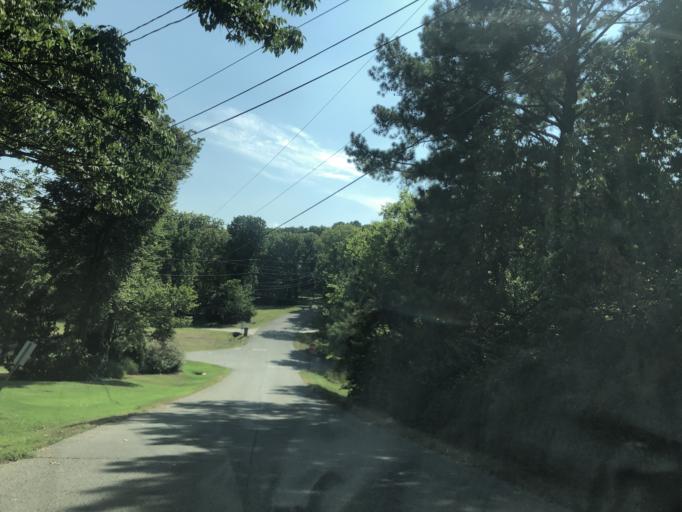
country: US
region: Tennessee
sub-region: Davidson County
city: Oak Hill
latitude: 36.0857
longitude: -86.8100
